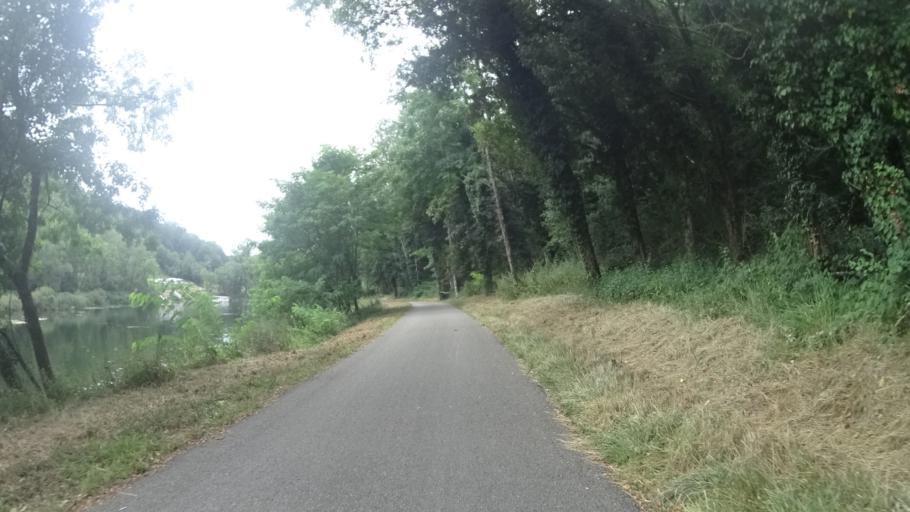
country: FR
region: Franche-Comte
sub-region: Departement du Doubs
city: Baume-les-Dames
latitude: 47.3409
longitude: 6.3401
